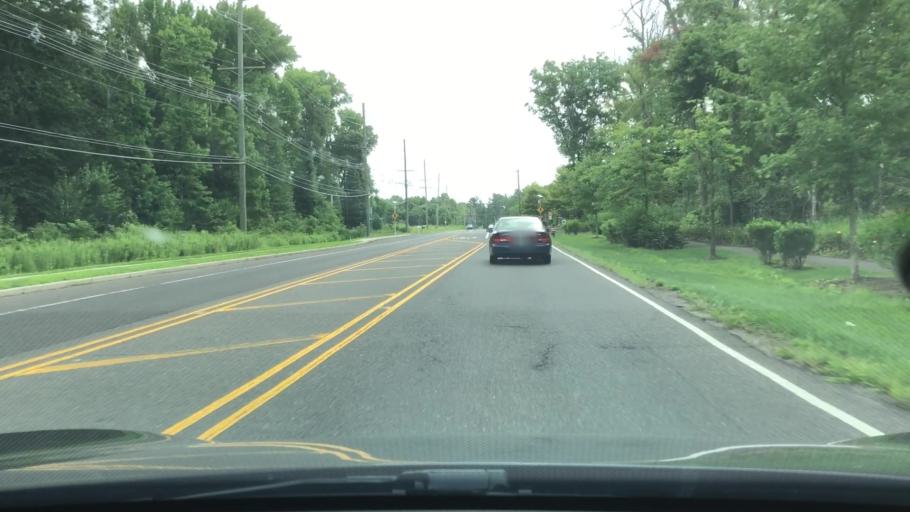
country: US
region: New Jersey
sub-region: Mercer County
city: Princeton Junction
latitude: 40.2947
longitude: -74.6573
